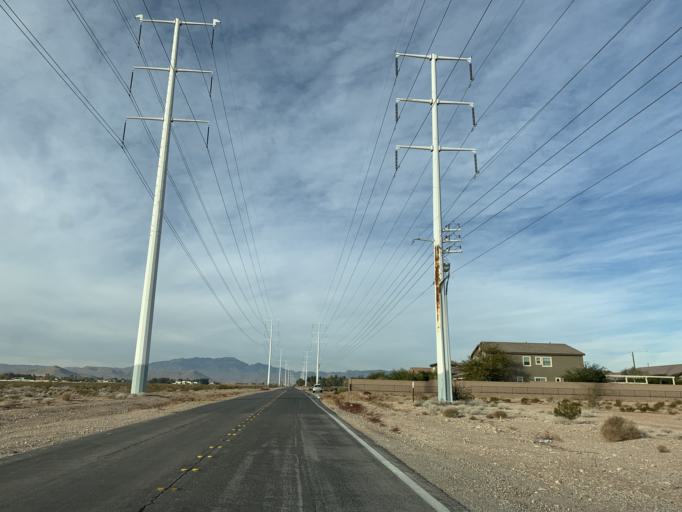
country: US
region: Nevada
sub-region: Clark County
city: Enterprise
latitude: 36.0028
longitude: -115.1838
